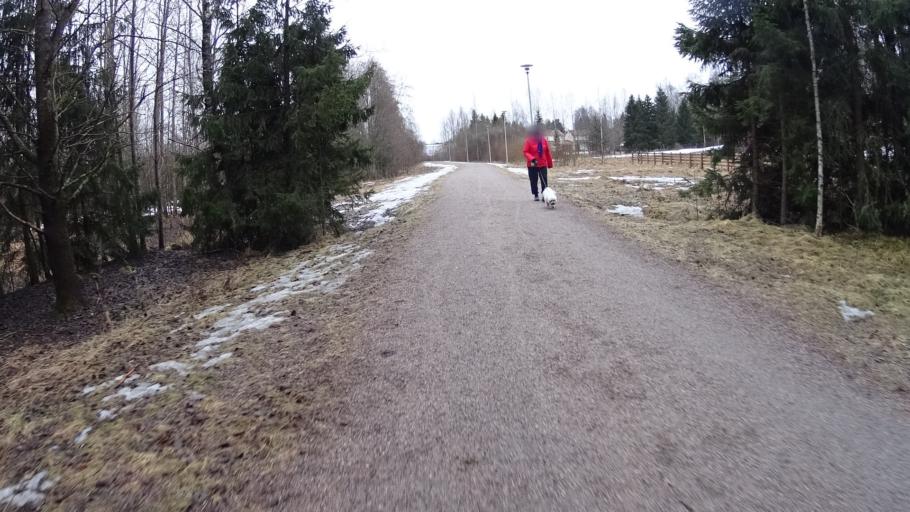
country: FI
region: Uusimaa
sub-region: Helsinki
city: Espoo
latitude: 60.2175
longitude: 24.6425
